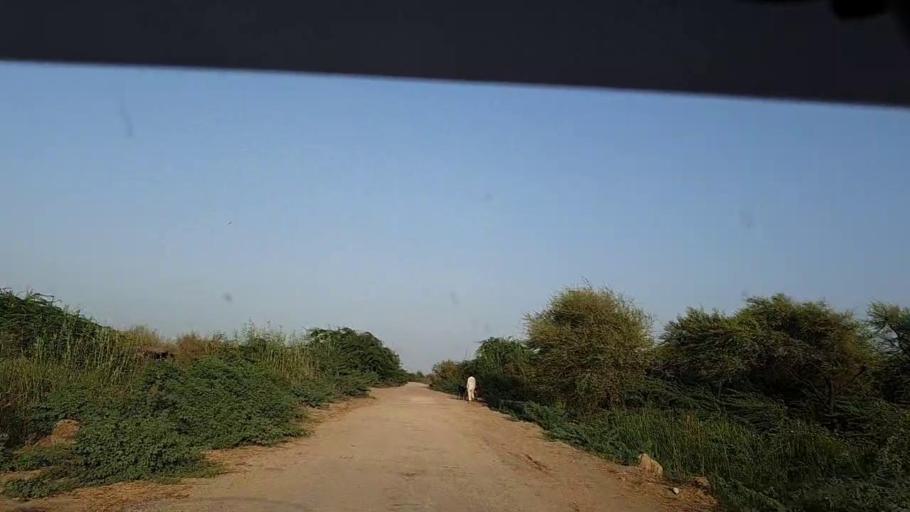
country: PK
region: Sindh
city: Kadhan
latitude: 24.5468
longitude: 68.9395
